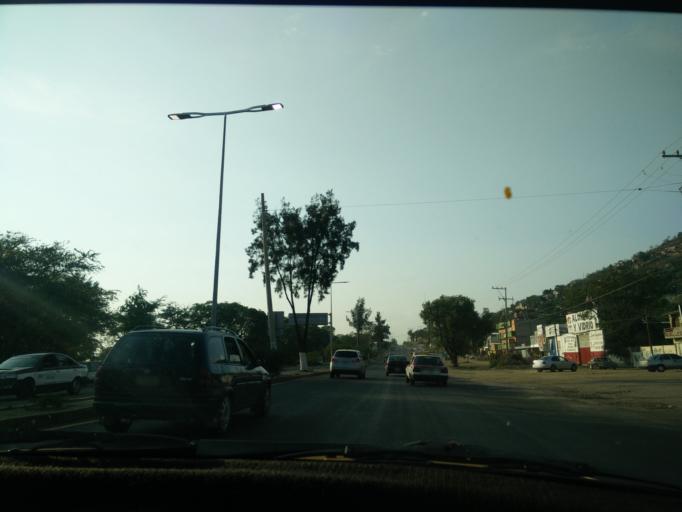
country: MX
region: Oaxaca
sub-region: Santa Maria Atzompa
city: San Jeronimo Yahuiche
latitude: 17.1043
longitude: -96.7529
